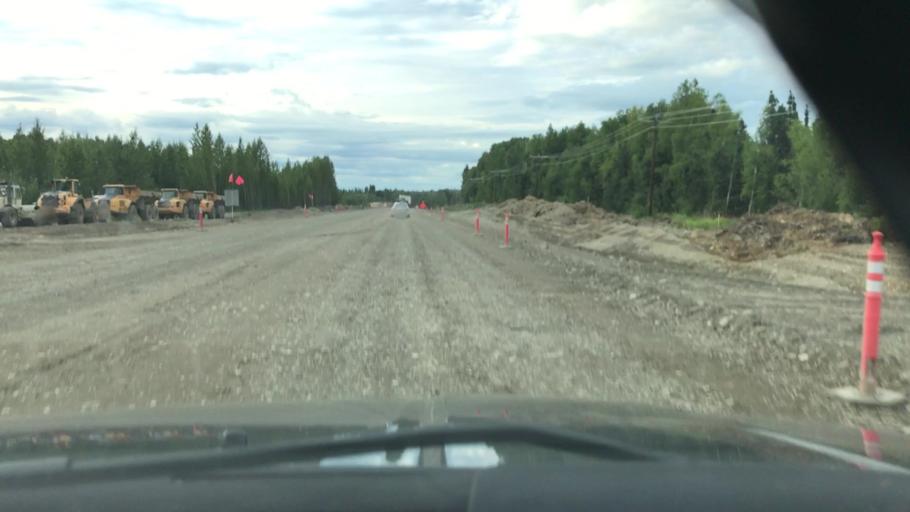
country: US
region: Alaska
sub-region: Matanuska-Susitna Borough
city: Y
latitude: 62.0908
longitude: -150.0615
